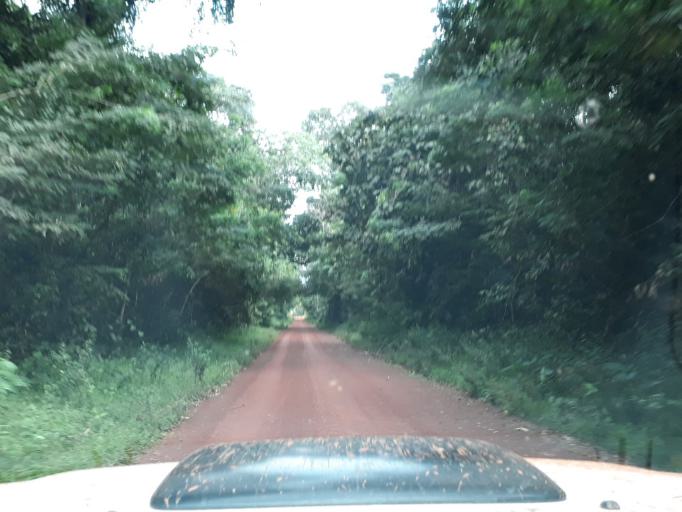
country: CD
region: Eastern Province
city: Buta
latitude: 2.2930
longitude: 25.0514
